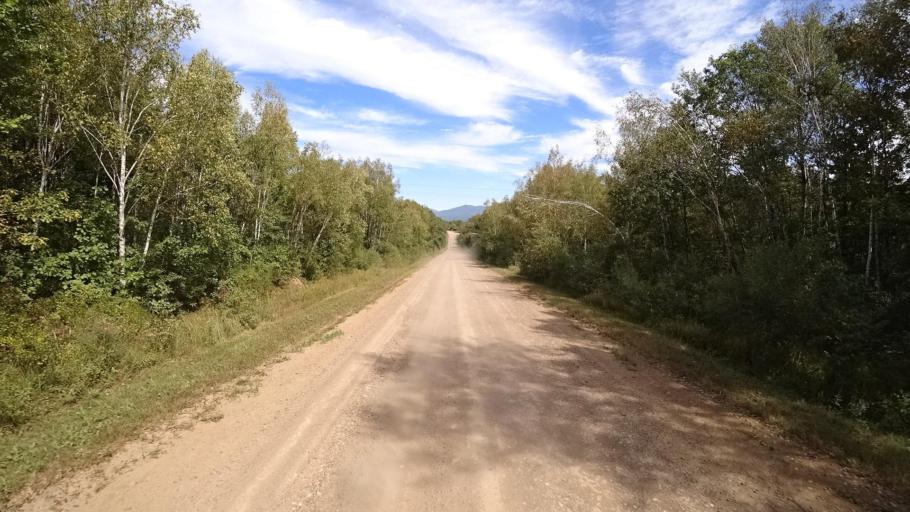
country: RU
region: Primorskiy
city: Yakovlevka
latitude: 44.7030
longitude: 133.6372
